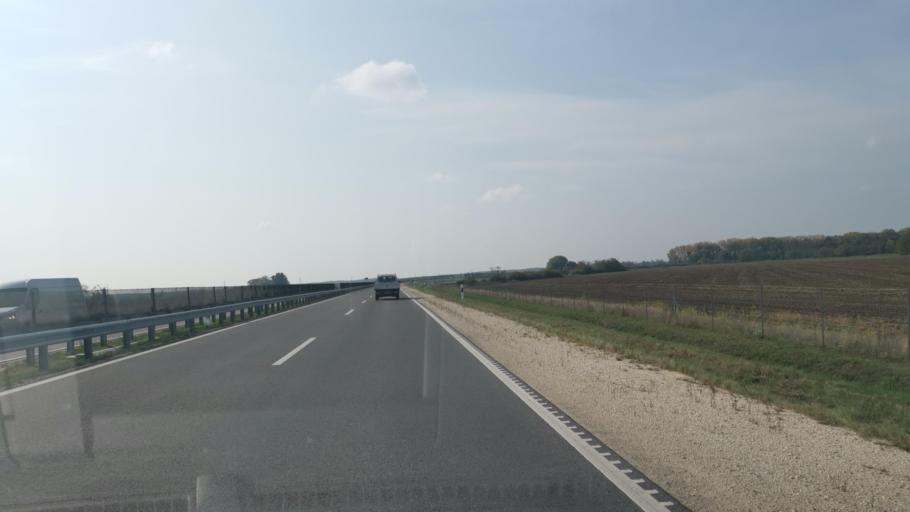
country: HU
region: Gyor-Moson-Sopron
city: Farad
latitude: 47.5756
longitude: 17.1547
